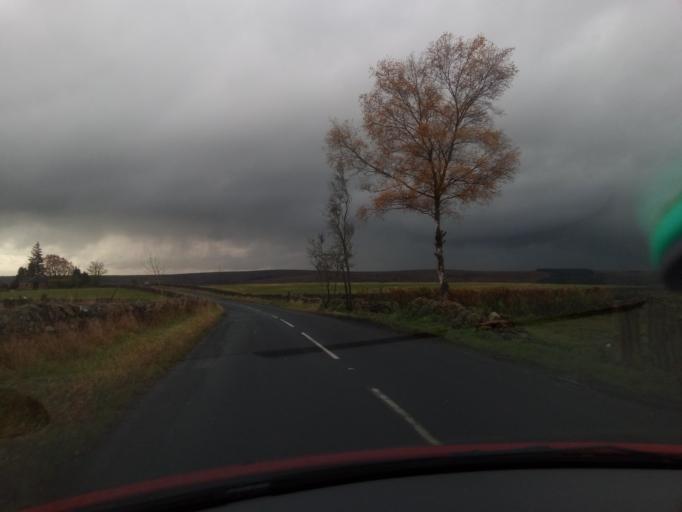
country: GB
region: England
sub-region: Northumberland
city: Corsenside
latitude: 55.1541
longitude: -2.2585
